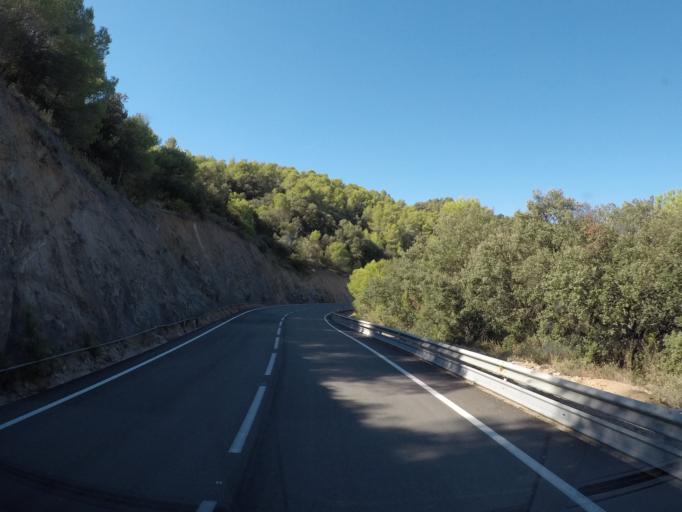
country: ES
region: Catalonia
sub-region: Provincia de Tarragona
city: Falset
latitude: 41.1666
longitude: 0.8194
